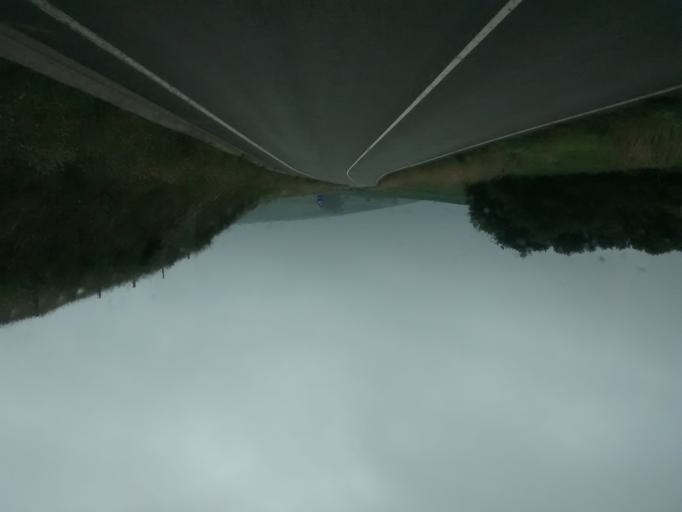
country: ES
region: Cantabria
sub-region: Provincia de Cantabria
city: Santillana
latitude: 43.4209
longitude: -4.0944
